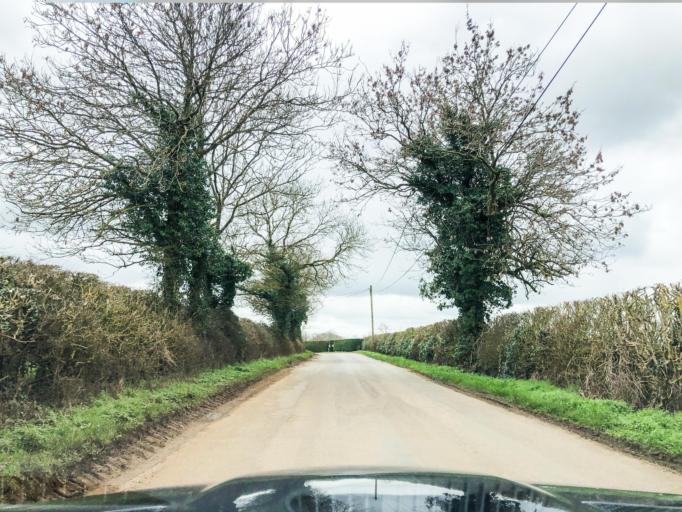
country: GB
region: England
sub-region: Oxfordshire
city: Hook Norton
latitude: 52.0883
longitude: -1.4833
